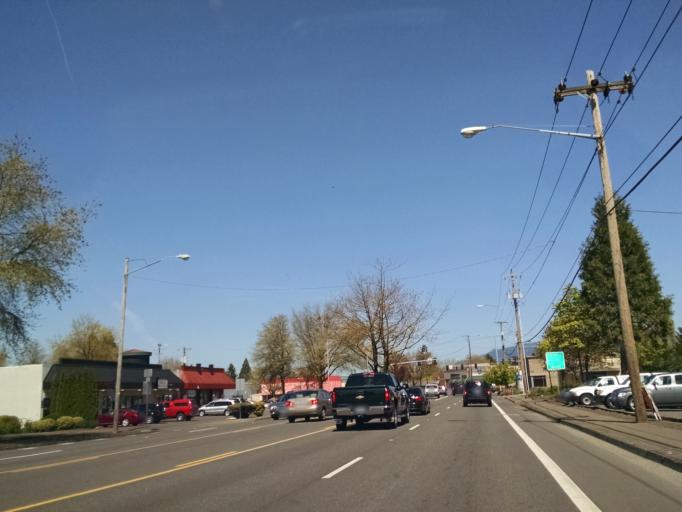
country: US
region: Oregon
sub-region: Lane County
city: Eugene
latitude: 44.0790
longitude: -123.0684
